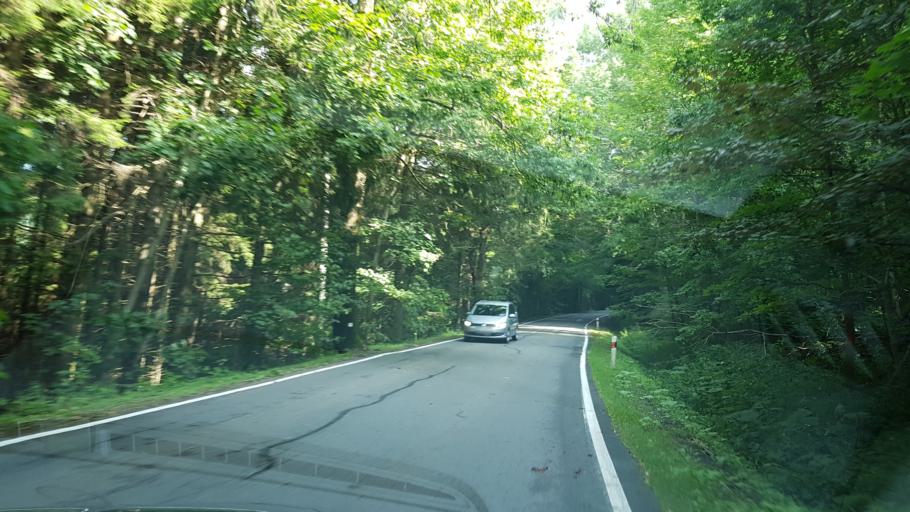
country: CZ
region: Olomoucky
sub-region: Okres Jesenik
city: Jesenik
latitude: 50.2158
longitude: 17.2491
